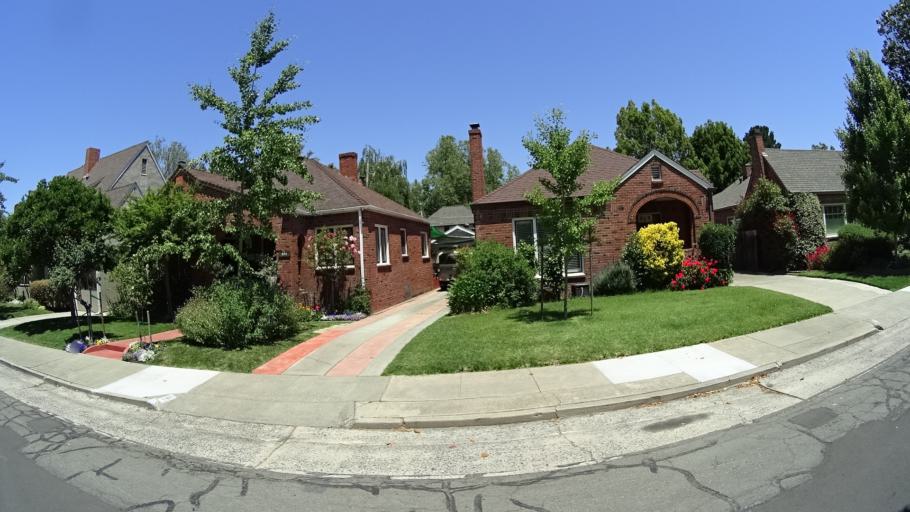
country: US
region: California
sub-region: Sacramento County
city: Sacramento
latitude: 38.5554
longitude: -121.5052
